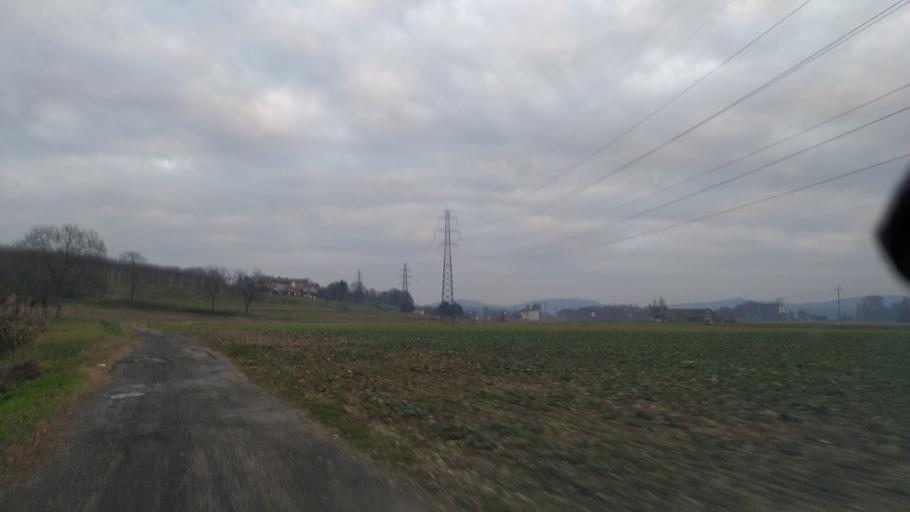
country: IT
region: Piedmont
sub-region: Provincia di Torino
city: Piverone
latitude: 45.4365
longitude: 8.0190
